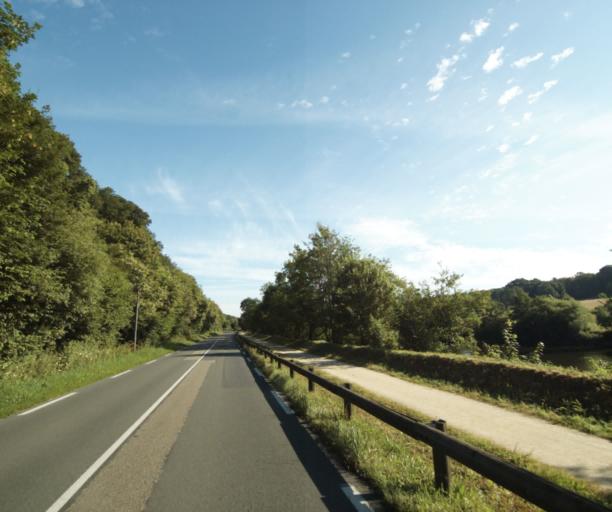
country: FR
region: Pays de la Loire
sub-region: Departement de la Mayenne
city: Laval
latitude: 48.0437
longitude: -0.7662
